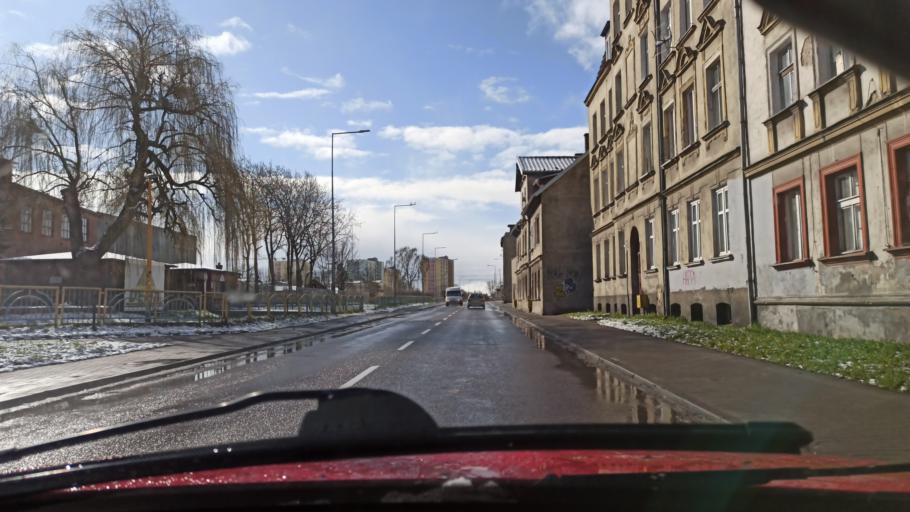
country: PL
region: Warmian-Masurian Voivodeship
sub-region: Powiat elblaski
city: Elblag
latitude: 54.1518
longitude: 19.4025
